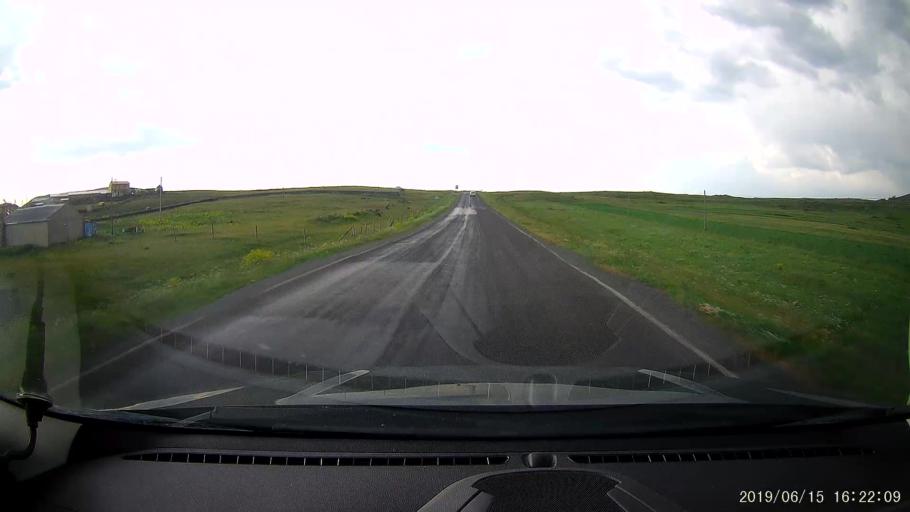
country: TR
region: Ardahan
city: Hanak
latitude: 41.1909
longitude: 42.8474
